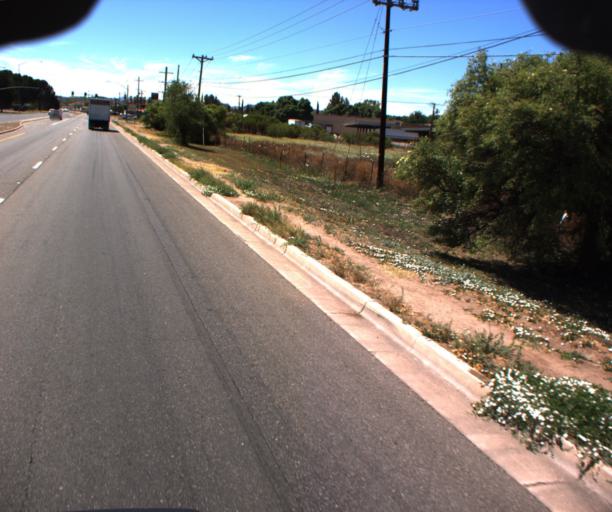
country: US
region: Arizona
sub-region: Santa Cruz County
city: Nogales
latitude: 31.3882
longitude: -110.9513
